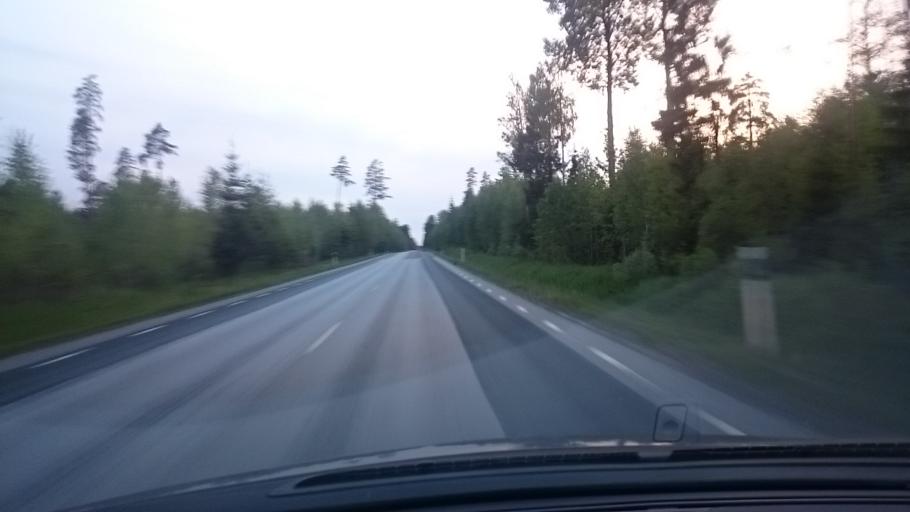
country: EE
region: Paernumaa
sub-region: Vaendra vald (alev)
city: Vandra
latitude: 58.8264
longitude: 25.1197
